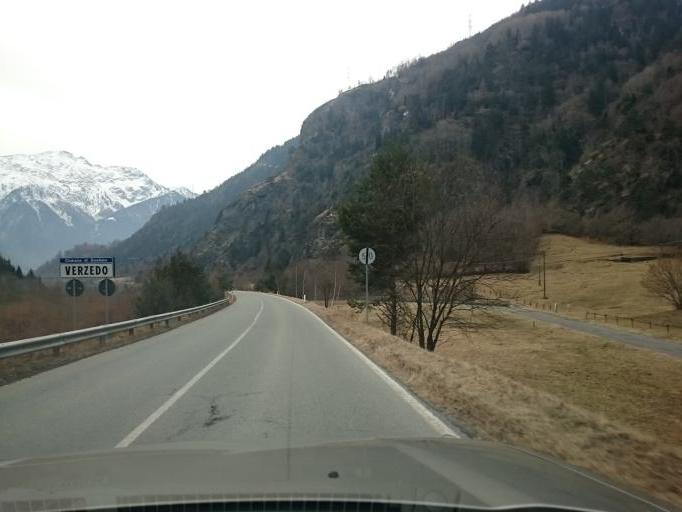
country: IT
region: Lombardy
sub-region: Provincia di Sondrio
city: Sondalo
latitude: 46.3668
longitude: 10.3559
